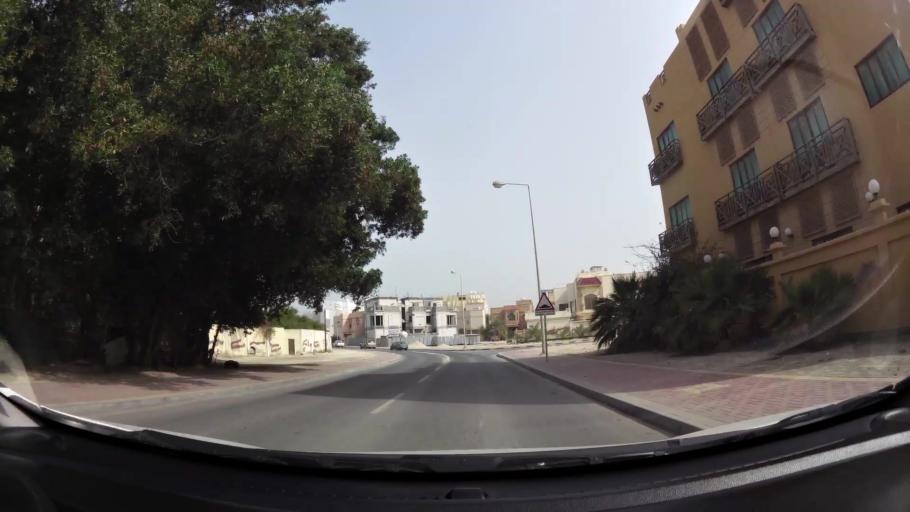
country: BH
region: Manama
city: Jidd Hafs
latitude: 26.2328
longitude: 50.5249
